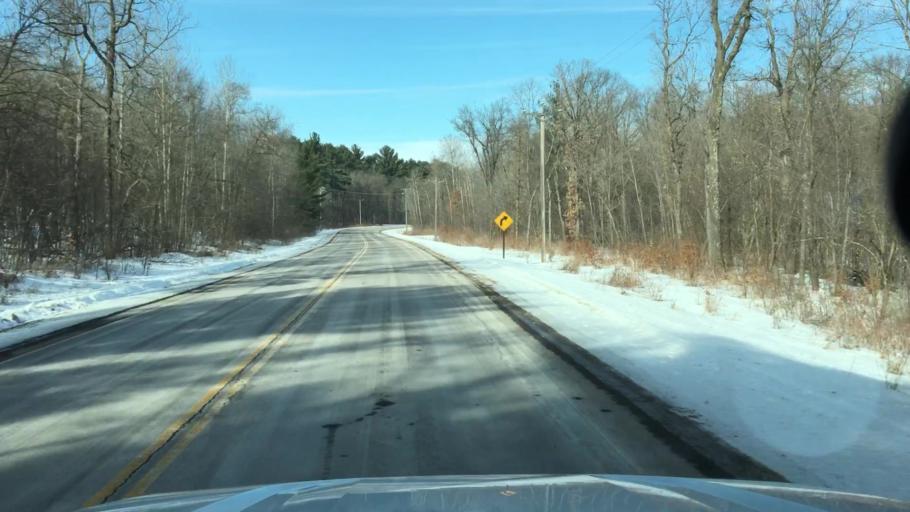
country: US
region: Wisconsin
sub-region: Polk County
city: Saint Croix Falls
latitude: 45.4643
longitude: -92.6838
